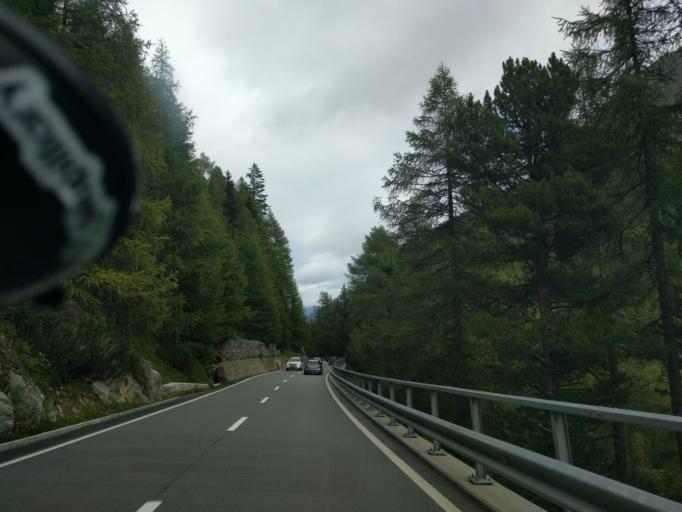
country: CH
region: Grisons
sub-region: Inn District
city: Zernez
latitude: 46.7514
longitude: 10.0133
